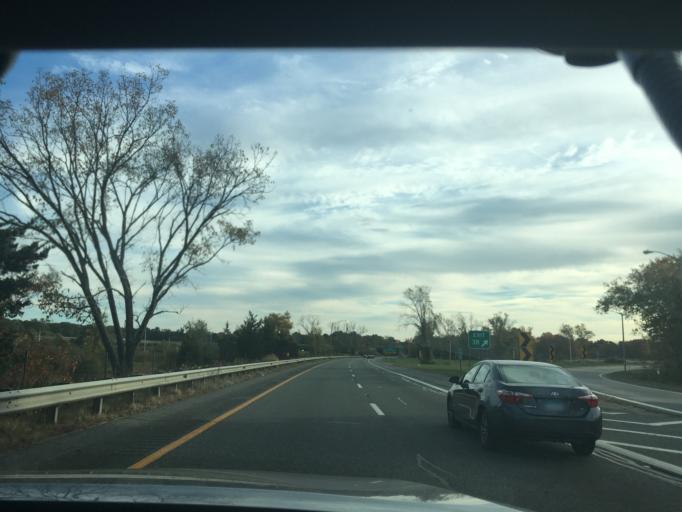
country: US
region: Rhode Island
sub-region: Providence County
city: Cranston
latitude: 41.7601
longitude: -71.4810
